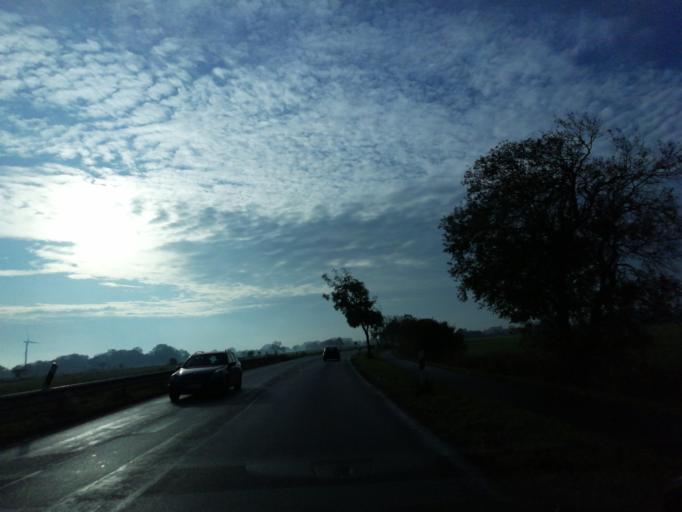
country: DE
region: Lower Saxony
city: Fedderwarden
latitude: 53.6073
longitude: 8.0448
